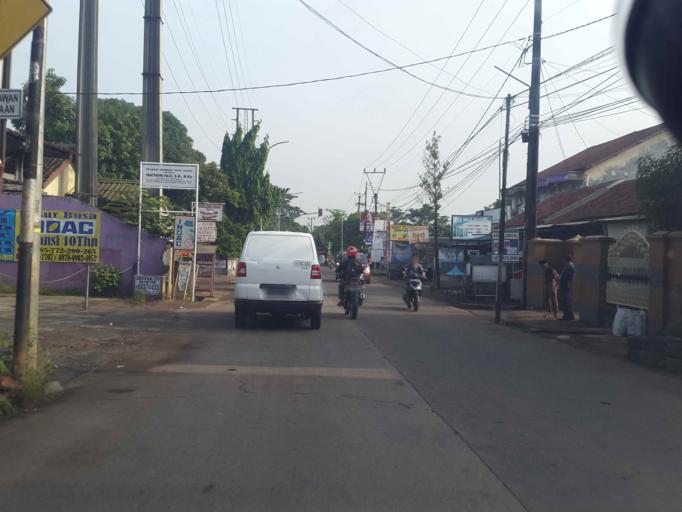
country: ID
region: West Java
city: Bekasi
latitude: -6.2985
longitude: 107.0302
